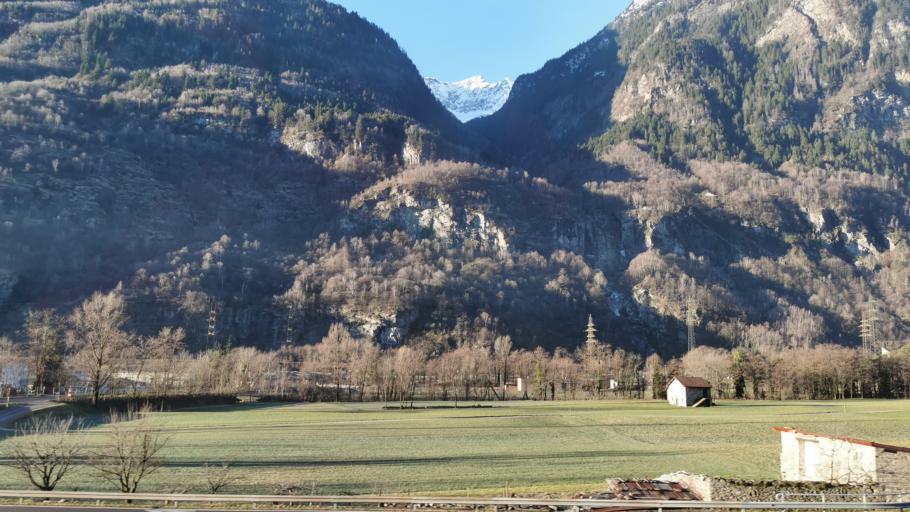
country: CH
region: Ticino
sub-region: Leventina District
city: Bodio
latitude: 46.3935
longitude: 8.8895
